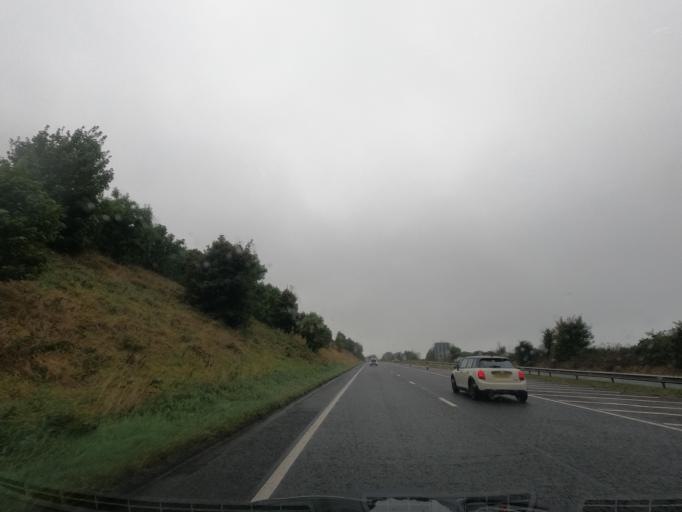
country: GB
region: England
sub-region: Redcar and Cleveland
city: South Bank
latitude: 54.5607
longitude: -1.1292
